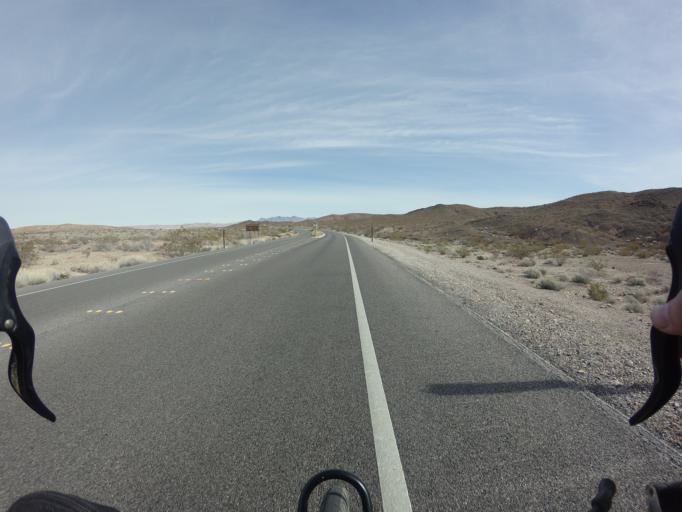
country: US
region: Nevada
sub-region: Clark County
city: Henderson
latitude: 36.1411
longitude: -114.8912
